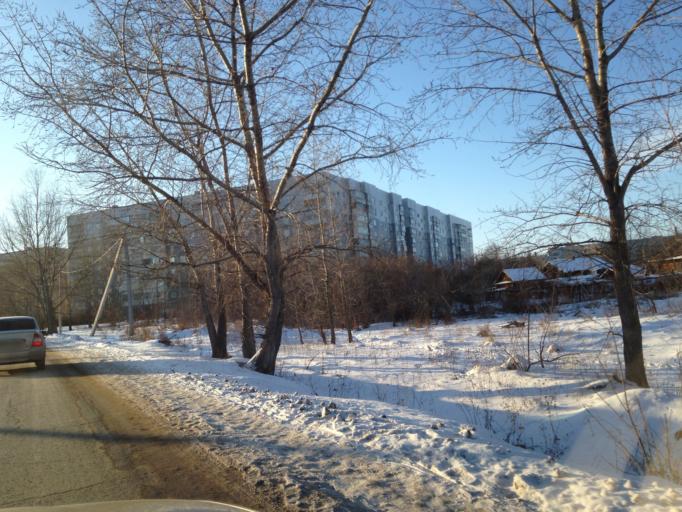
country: RU
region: Ulyanovsk
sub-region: Ulyanovskiy Rayon
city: Ulyanovsk
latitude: 54.3230
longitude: 48.4808
